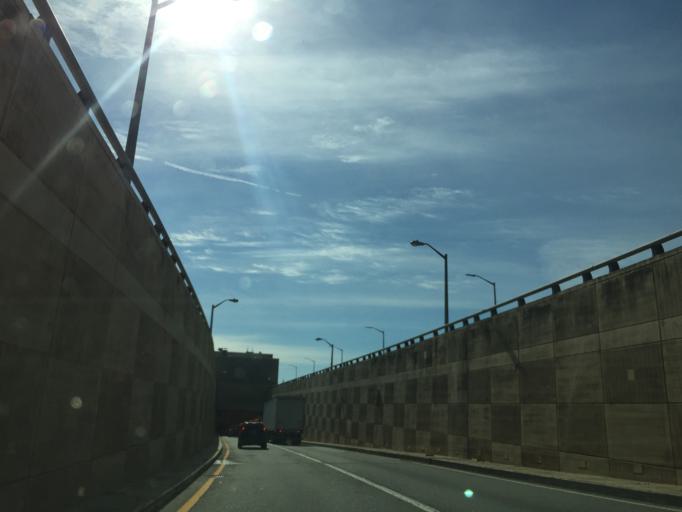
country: US
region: Virginia
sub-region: City of Hampton
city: East Hampton
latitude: 37.0016
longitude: -76.3193
